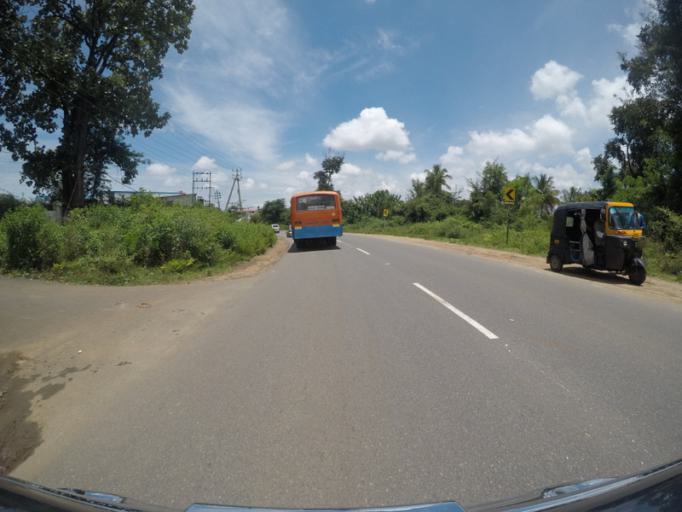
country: IN
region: Karnataka
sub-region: Kodagu
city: Kushalnagar
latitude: 12.4484
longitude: 75.9416
